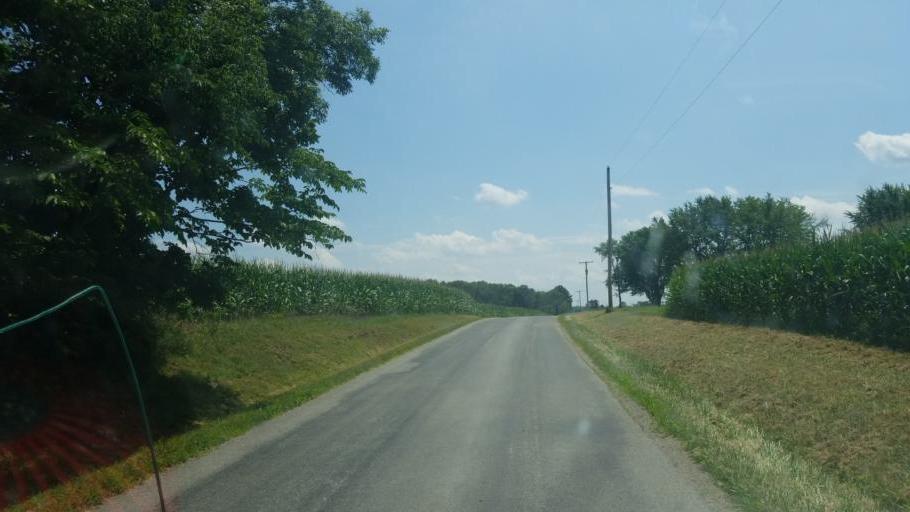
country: US
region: Ohio
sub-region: Crawford County
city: Crestline
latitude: 40.7321
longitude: -82.7216
